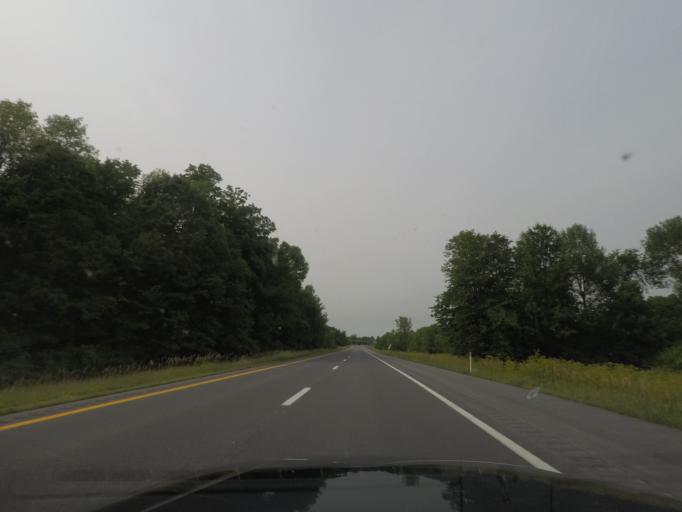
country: US
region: New York
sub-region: Clinton County
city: Champlain
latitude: 44.8660
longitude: -73.4498
